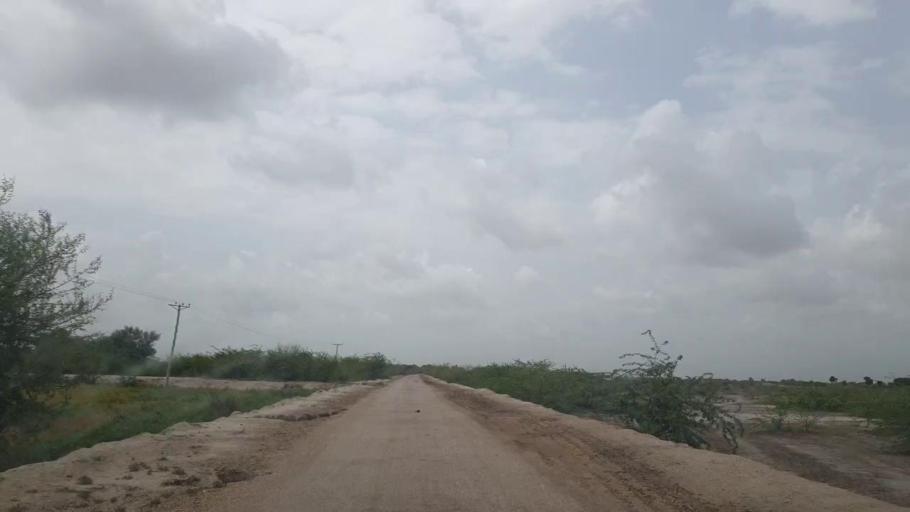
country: PK
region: Sindh
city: Naukot
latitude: 24.9486
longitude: 69.2584
